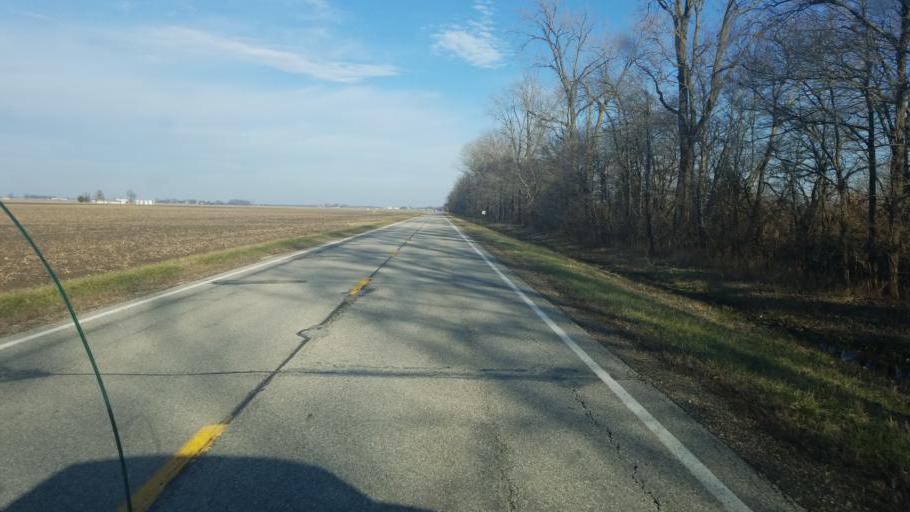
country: US
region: Illinois
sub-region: Edwards County
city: Grayville
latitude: 38.3248
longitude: -87.9142
